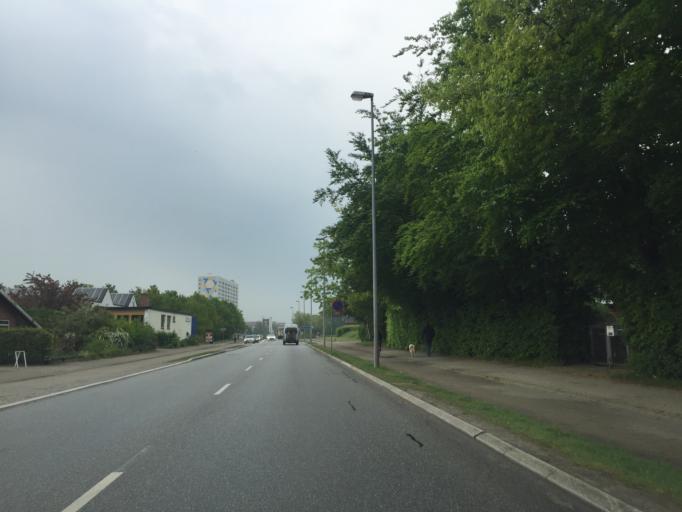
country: DK
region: Capital Region
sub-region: Rodovre Kommune
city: Rodovre
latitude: 55.6719
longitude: 12.4349
